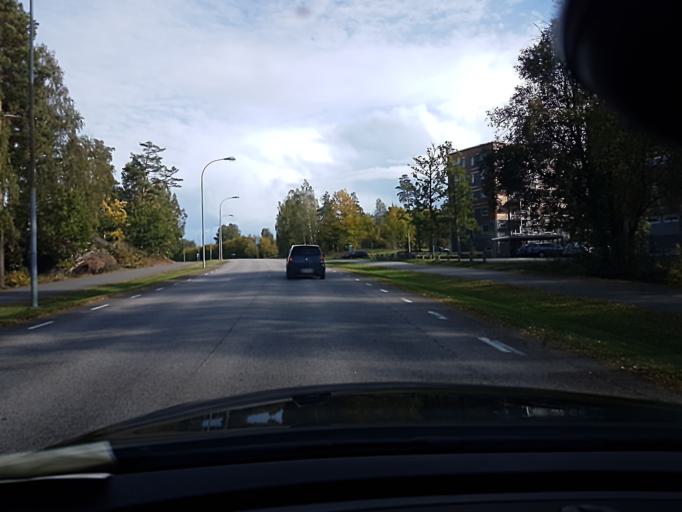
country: SE
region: Kronoberg
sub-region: Vaxjo Kommun
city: Vaexjoe
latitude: 56.8542
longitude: 14.8097
